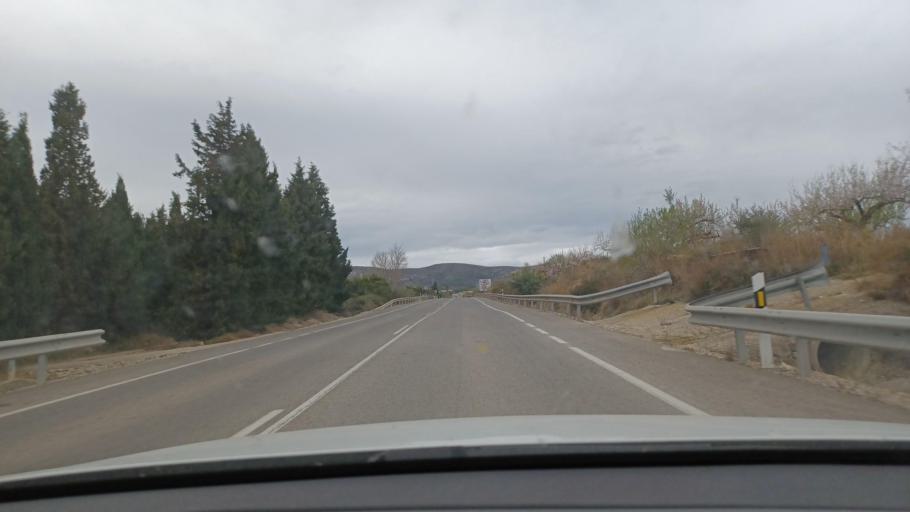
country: ES
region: Valencia
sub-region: Provincia de Castello
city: Traiguera
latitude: 40.5227
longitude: 0.3045
